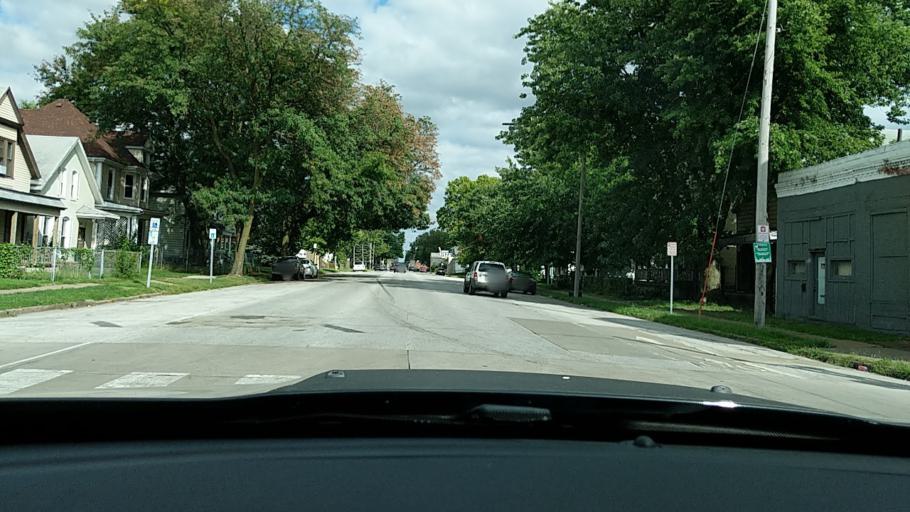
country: US
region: Iowa
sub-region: Scott County
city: Davenport
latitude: 41.5223
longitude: -90.6012
